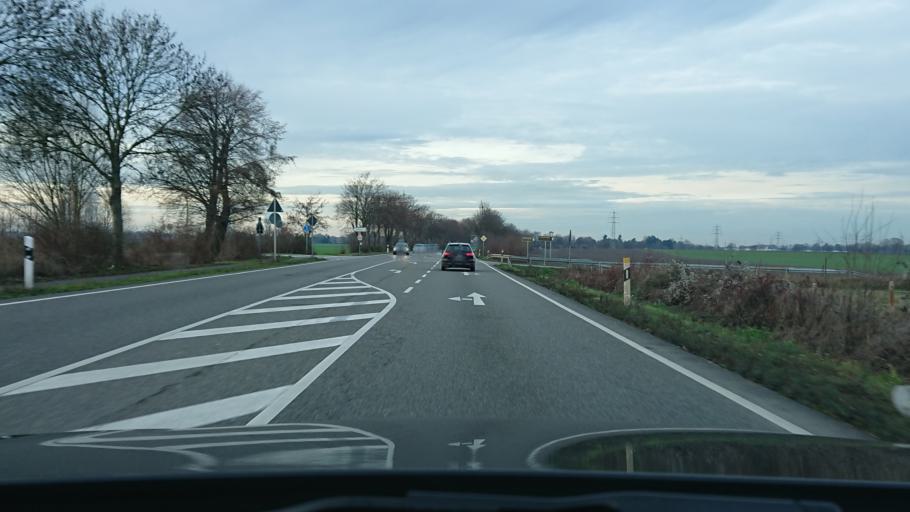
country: DE
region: North Rhine-Westphalia
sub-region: Regierungsbezirk Koln
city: Frechen
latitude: 50.9442
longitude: 6.8091
